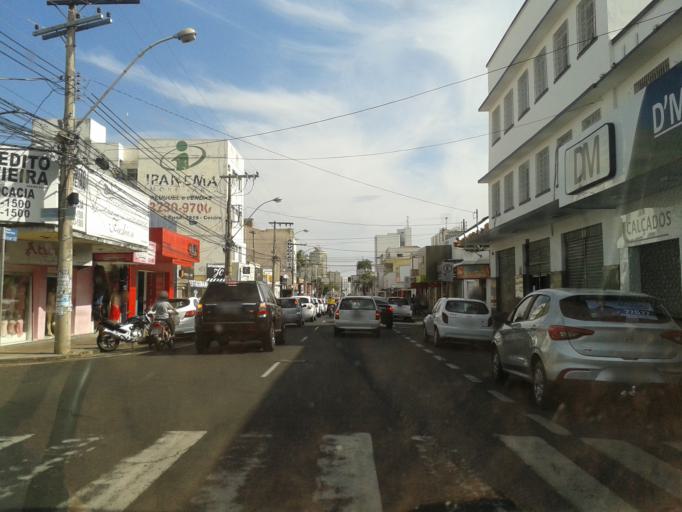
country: BR
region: Minas Gerais
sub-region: Uberlandia
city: Uberlandia
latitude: -18.9141
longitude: -48.2727
